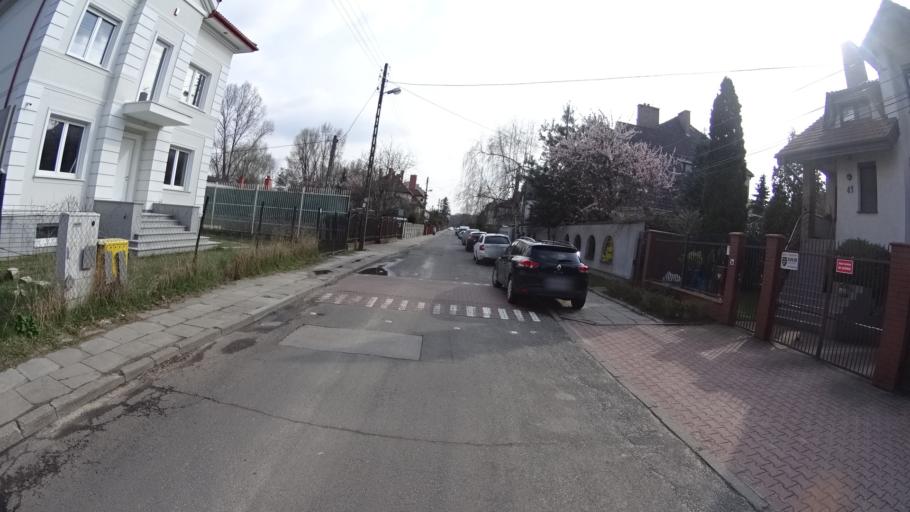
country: PL
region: Masovian Voivodeship
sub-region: Warszawa
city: Bemowo
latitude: 52.2340
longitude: 20.9221
